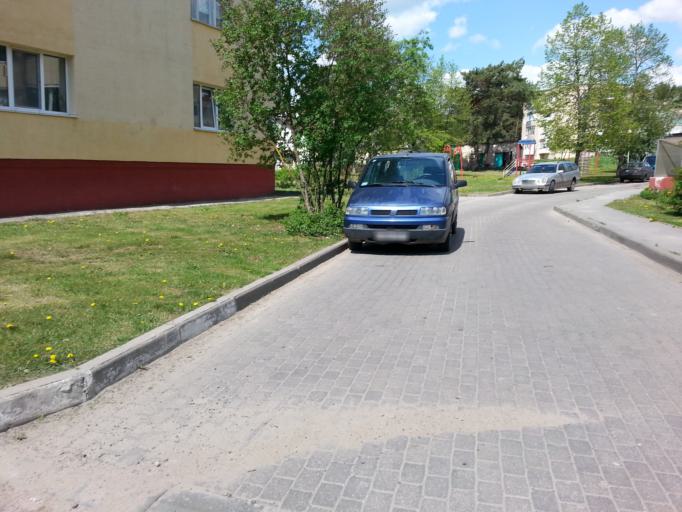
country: BY
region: Minsk
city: Narach
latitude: 54.9077
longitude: 26.7058
